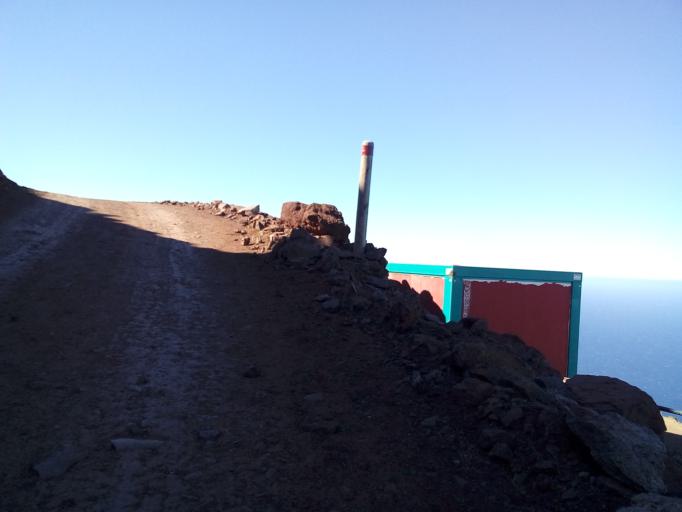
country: ES
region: Canary Islands
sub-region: Provincia de Santa Cruz de Tenerife
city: Vallehermosa
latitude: 28.1286
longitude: -17.3276
